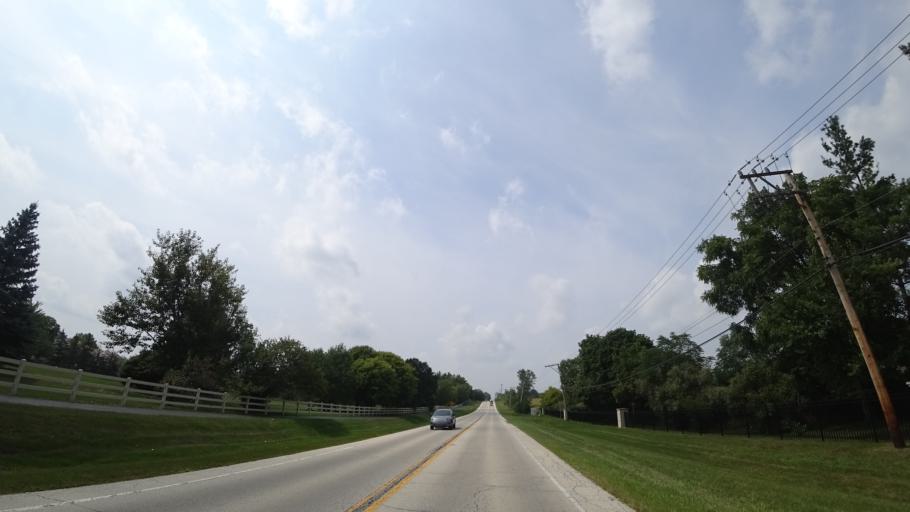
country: US
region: Illinois
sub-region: Will County
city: Goodings Grove
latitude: 41.6150
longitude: -87.9049
